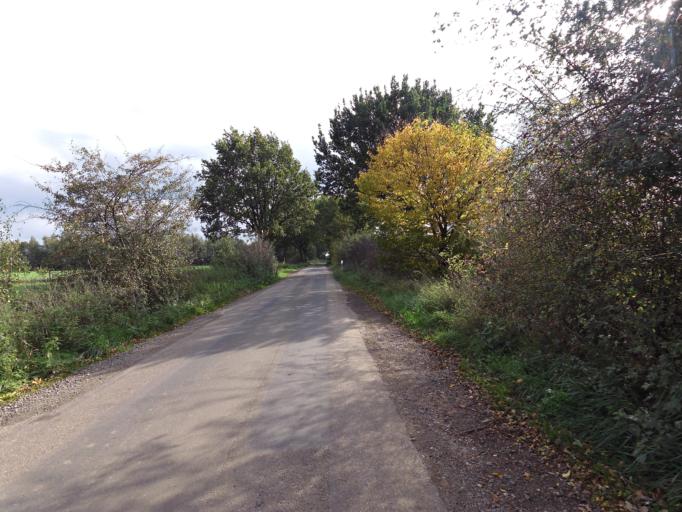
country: DE
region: North Rhine-Westphalia
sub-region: Regierungsbezirk Munster
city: Isselburg
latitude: 51.8236
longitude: 6.4805
